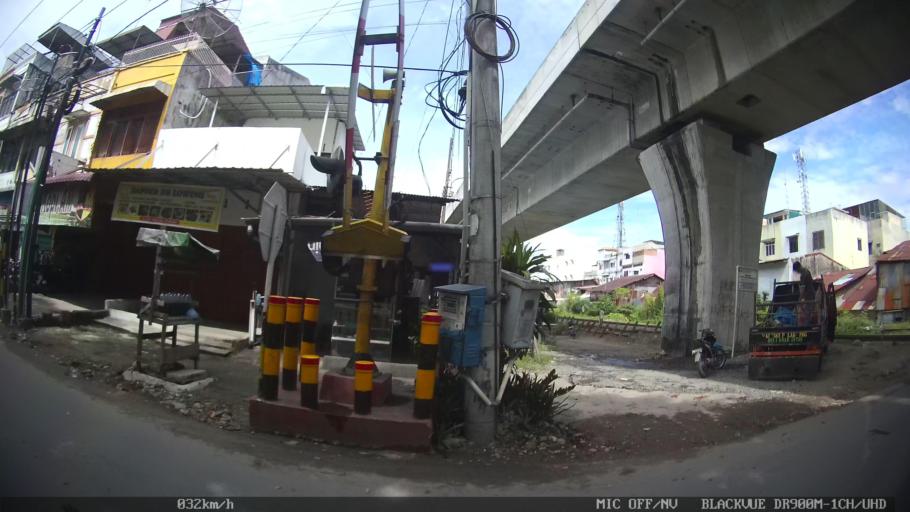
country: ID
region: North Sumatra
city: Medan
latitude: 3.5886
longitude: 98.7058
